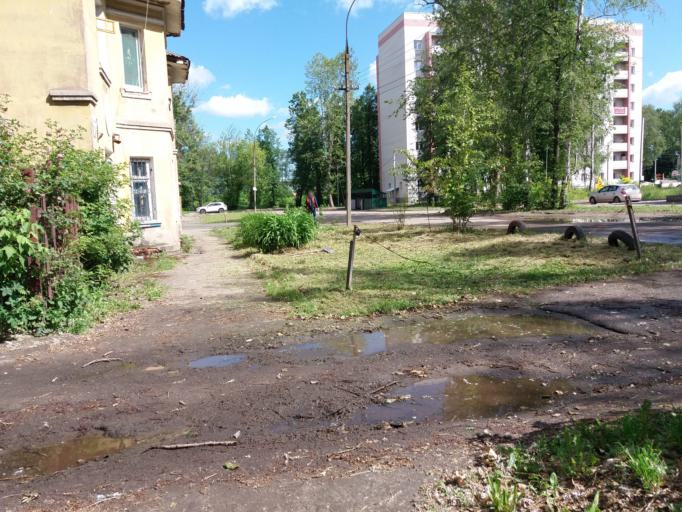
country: RU
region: Jaroslavl
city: Yaroslavl
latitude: 57.6414
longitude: 39.8439
